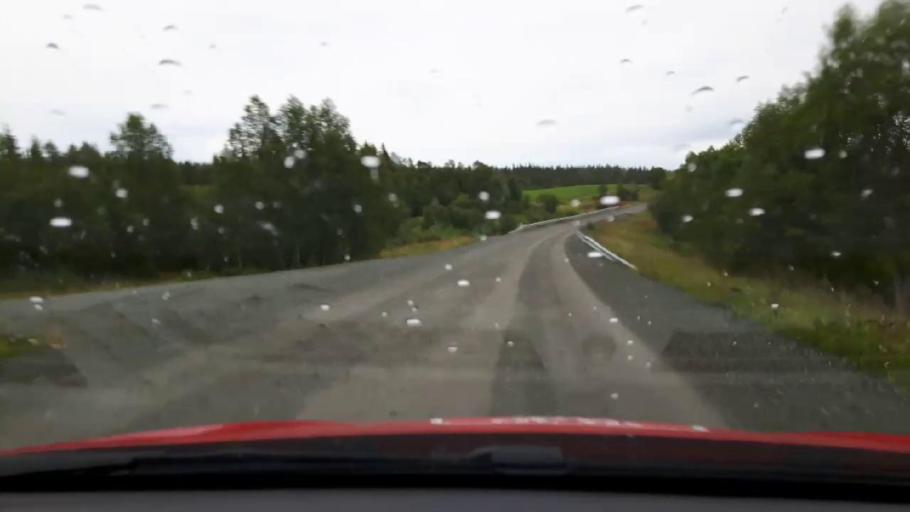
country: SE
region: Jaemtland
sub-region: Are Kommun
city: Are
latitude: 63.4782
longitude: 12.5478
